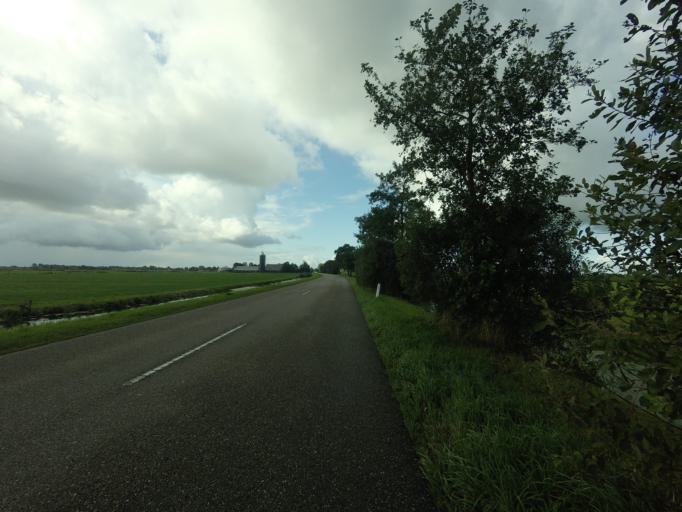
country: NL
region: Friesland
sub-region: Gemeente Boarnsterhim
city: Warten
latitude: 53.1569
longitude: 5.9152
